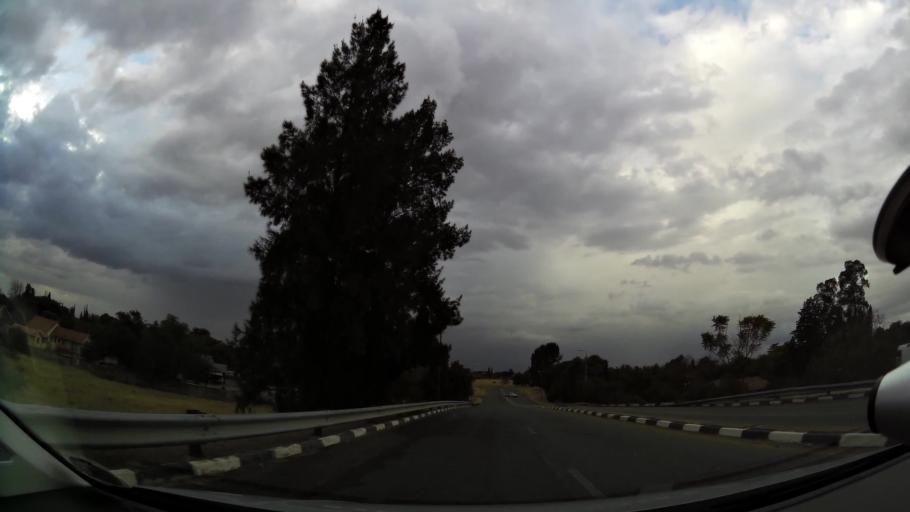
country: ZA
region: Orange Free State
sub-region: Lejweleputswa District Municipality
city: Welkom
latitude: -27.9580
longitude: 26.7277
